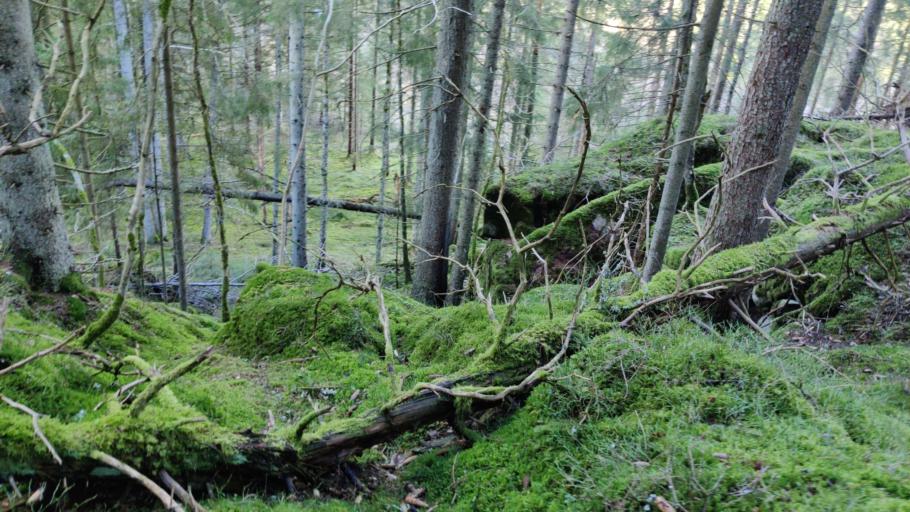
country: SE
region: Vaestra Goetaland
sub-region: Uddevalla Kommun
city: Uddevalla
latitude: 58.3485
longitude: 11.9683
